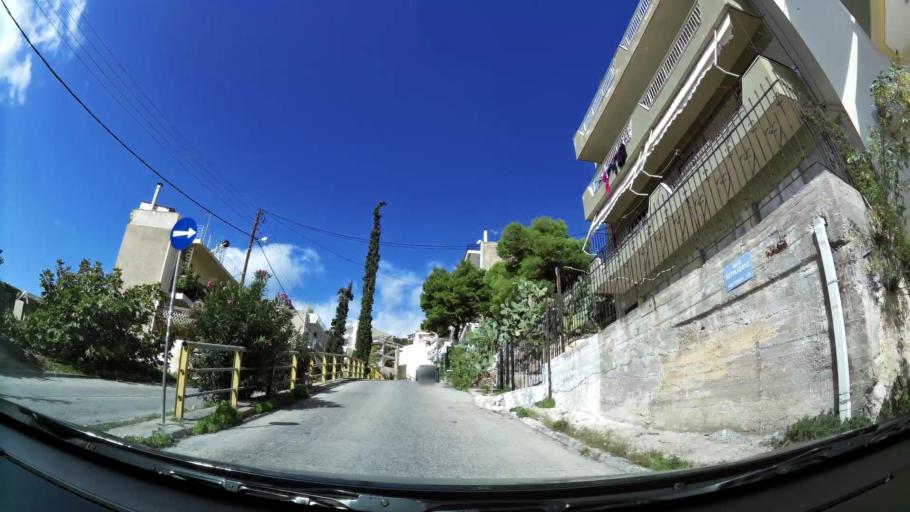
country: GR
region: Attica
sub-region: Nomos Piraios
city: Perama
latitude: 37.9666
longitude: 23.5762
